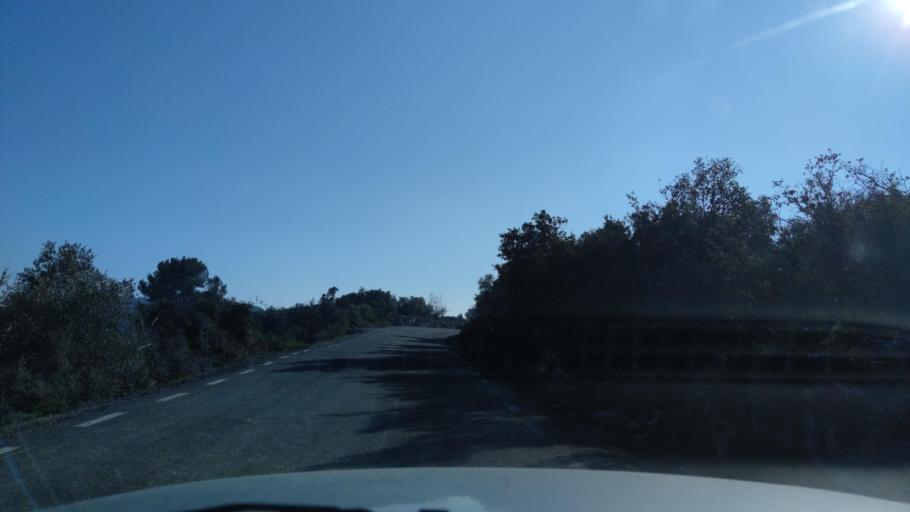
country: ES
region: Catalonia
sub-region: Provincia de Lleida
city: Torrebesses
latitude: 41.4453
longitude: 0.5584
